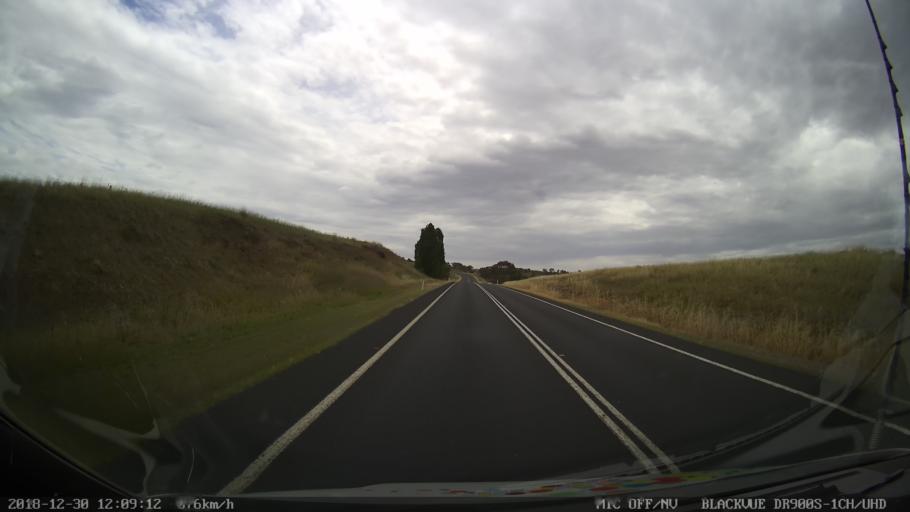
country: AU
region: New South Wales
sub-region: Snowy River
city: Jindabyne
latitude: -36.3875
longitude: 148.5990
